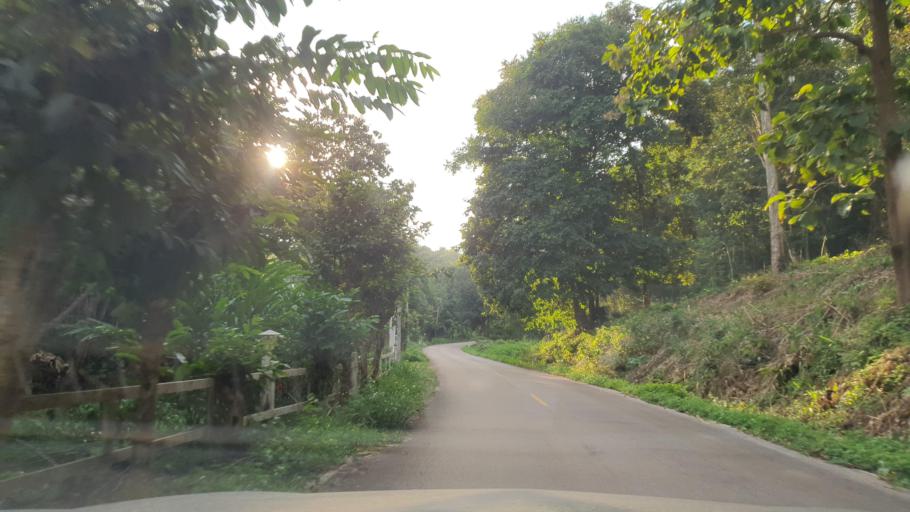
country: TH
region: Chiang Mai
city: Mae On
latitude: 18.8722
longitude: 99.2520
